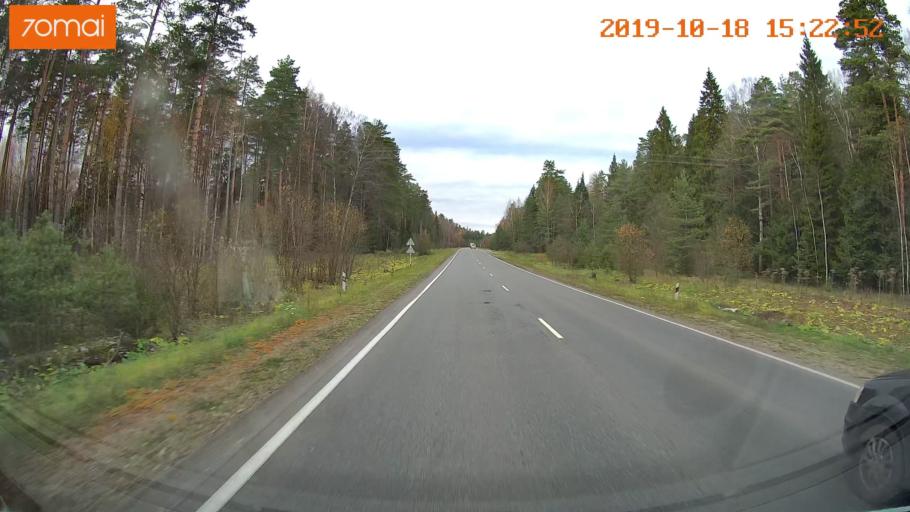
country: RU
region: Vladimir
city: Anopino
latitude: 55.7126
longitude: 40.7276
